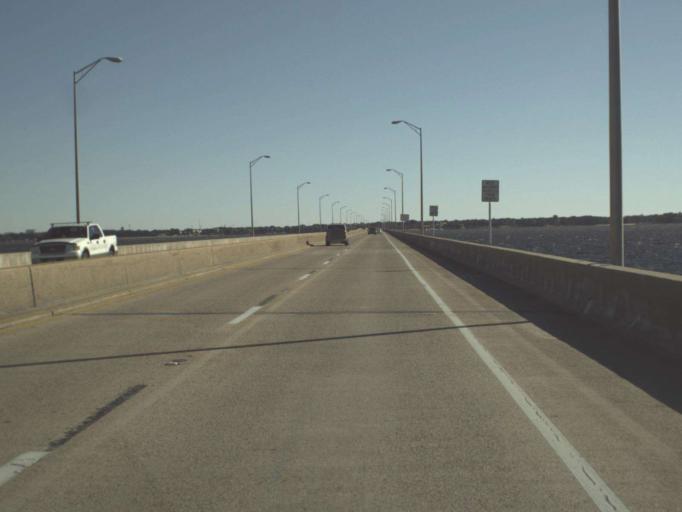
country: US
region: Florida
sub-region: Santa Rosa County
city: Gulf Breeze
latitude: 30.3874
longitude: -87.1825
